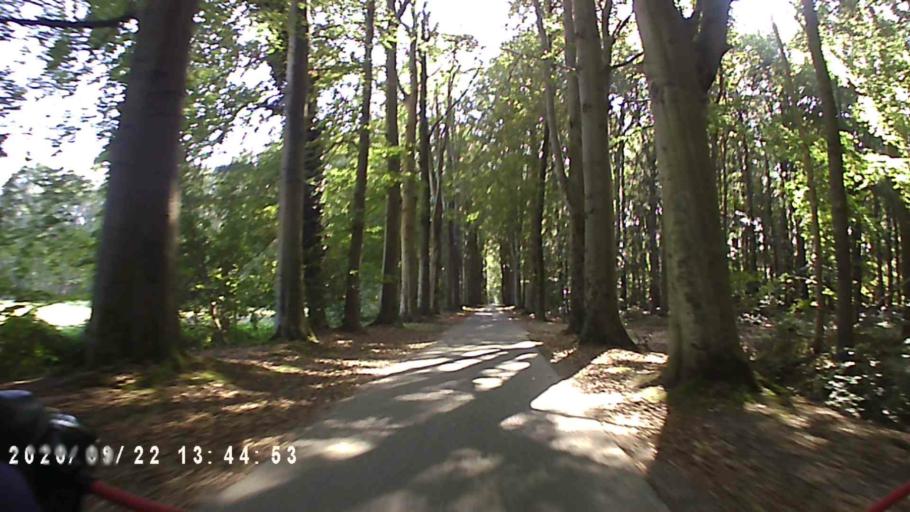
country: NL
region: Groningen
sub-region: Gemeente Leek
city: Leek
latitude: 53.1484
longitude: 6.4060
